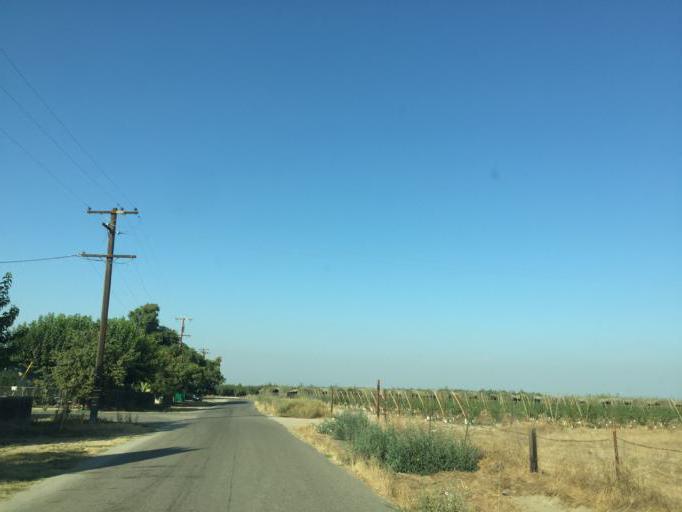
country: US
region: California
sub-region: Tulare County
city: London
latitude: 36.4538
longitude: -119.4837
